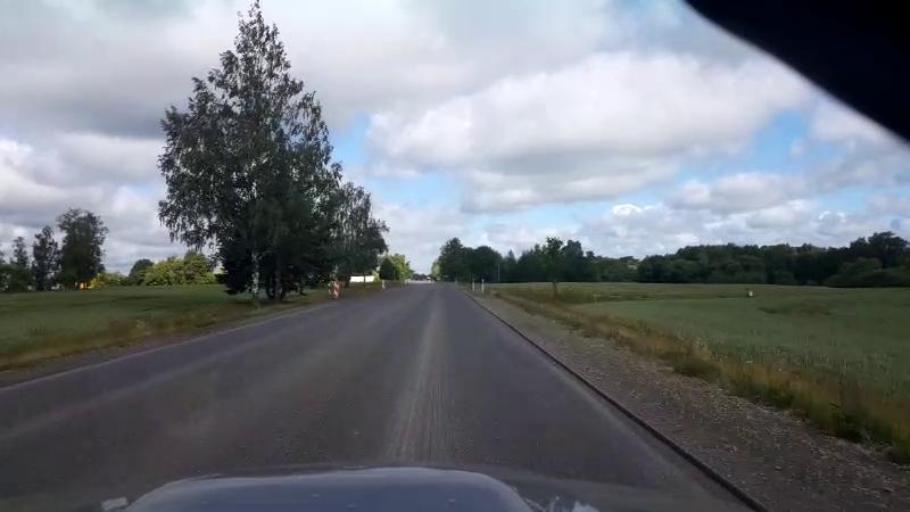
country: LV
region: Bauskas Rajons
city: Bauska
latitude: 56.3190
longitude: 24.3220
